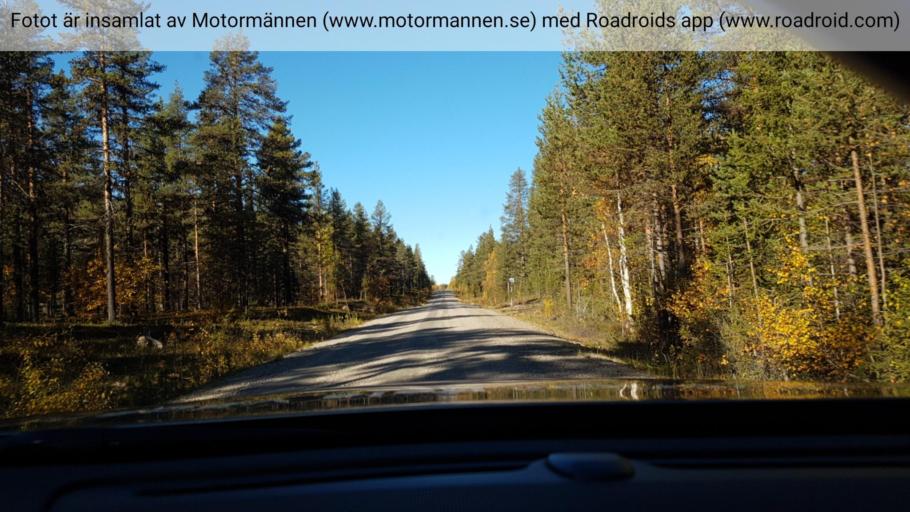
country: SE
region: Norrbotten
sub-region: Gallivare Kommun
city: Gaellivare
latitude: 66.6405
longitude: 21.0130
